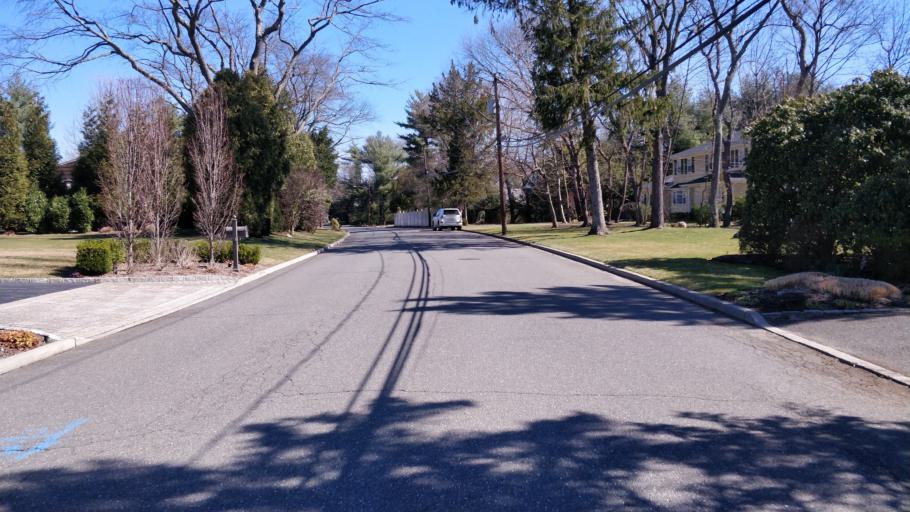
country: US
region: New York
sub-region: Nassau County
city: Syosset
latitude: 40.8355
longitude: -73.5132
